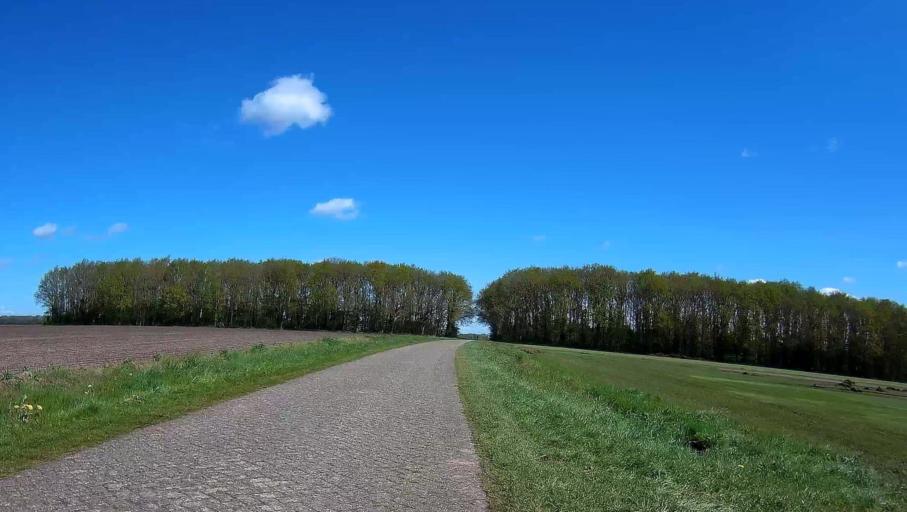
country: NL
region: Drenthe
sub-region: Gemeente Borger-Odoorn
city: Borger
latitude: 52.9350
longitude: 6.7950
